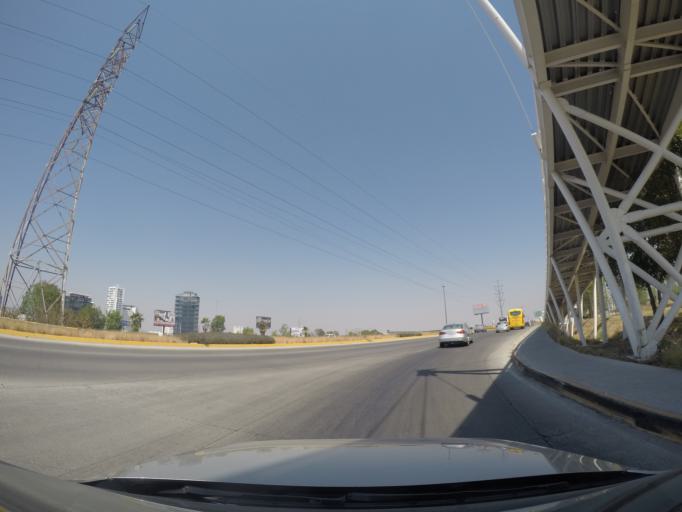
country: MX
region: Puebla
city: Tlazcalancingo
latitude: 19.0179
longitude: -98.2484
